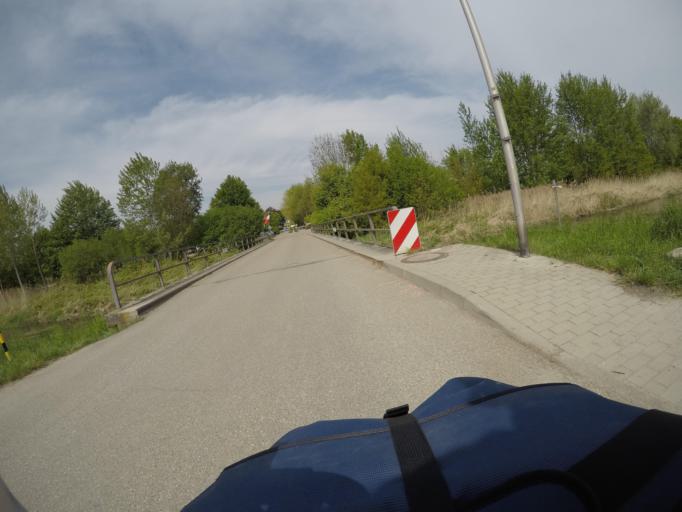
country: DE
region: Baden-Wuerttemberg
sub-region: Karlsruhe Region
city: Schwarzach
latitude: 48.7728
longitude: 8.0411
